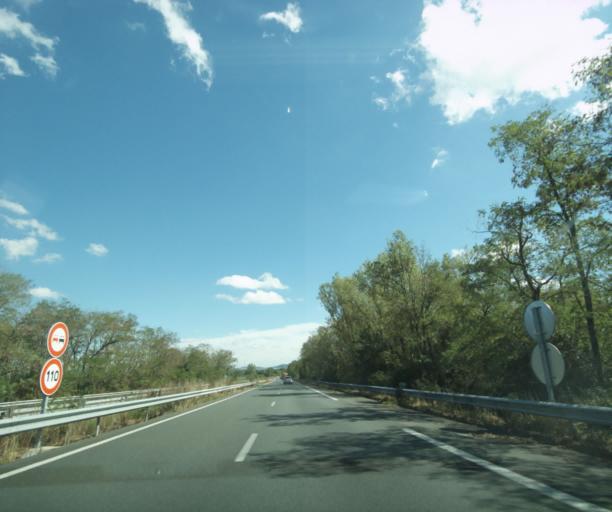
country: FR
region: Aquitaine
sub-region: Departement du Lot-et-Garonne
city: Fourques-sur-Garonne
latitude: 44.3783
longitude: 0.2189
